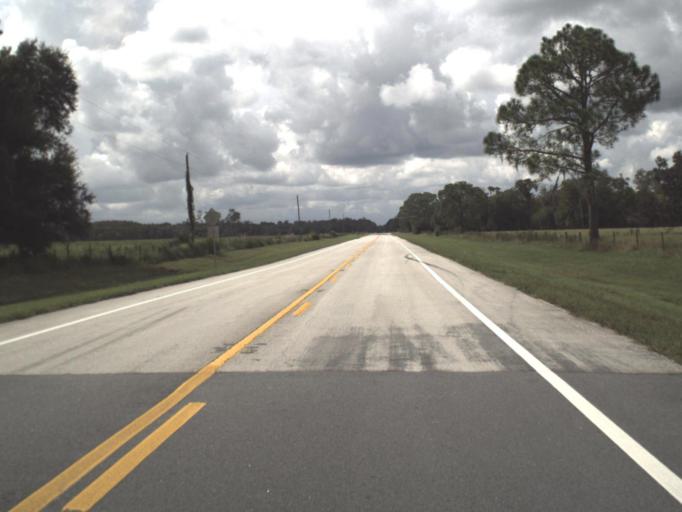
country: US
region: Florida
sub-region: DeSoto County
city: Nocatee
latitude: 27.2005
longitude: -81.9923
